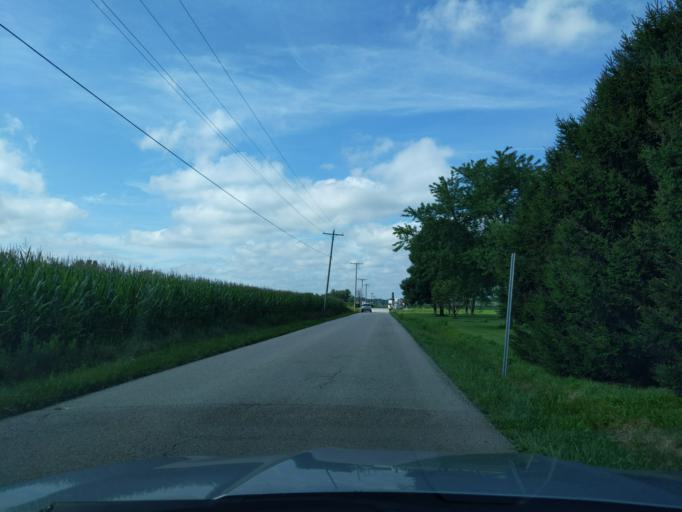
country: US
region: Indiana
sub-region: Ripley County
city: Batesville
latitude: 39.3107
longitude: -85.3477
